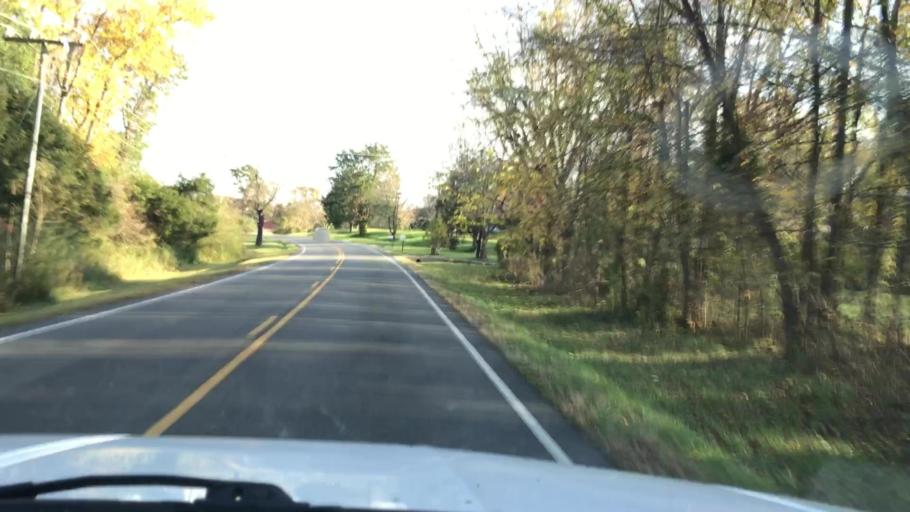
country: US
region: Virginia
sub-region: Goochland County
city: Goochland
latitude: 37.6397
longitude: -77.8141
